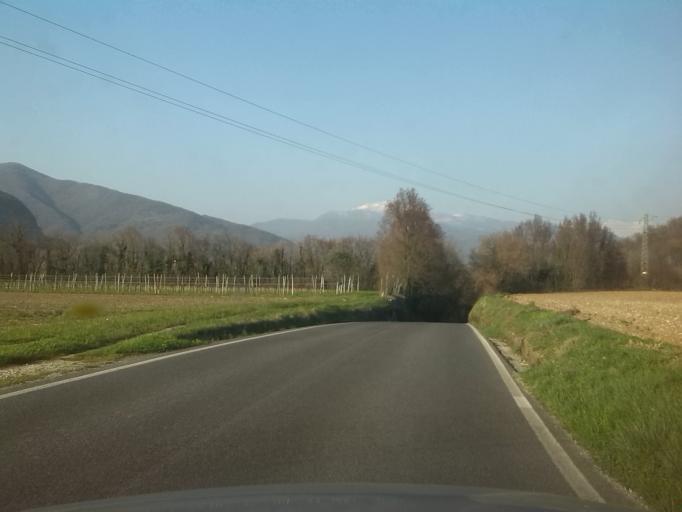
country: IT
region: Friuli Venezia Giulia
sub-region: Provincia di Udine
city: San Pietro al Natisone
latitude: 46.1040
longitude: 13.4709
